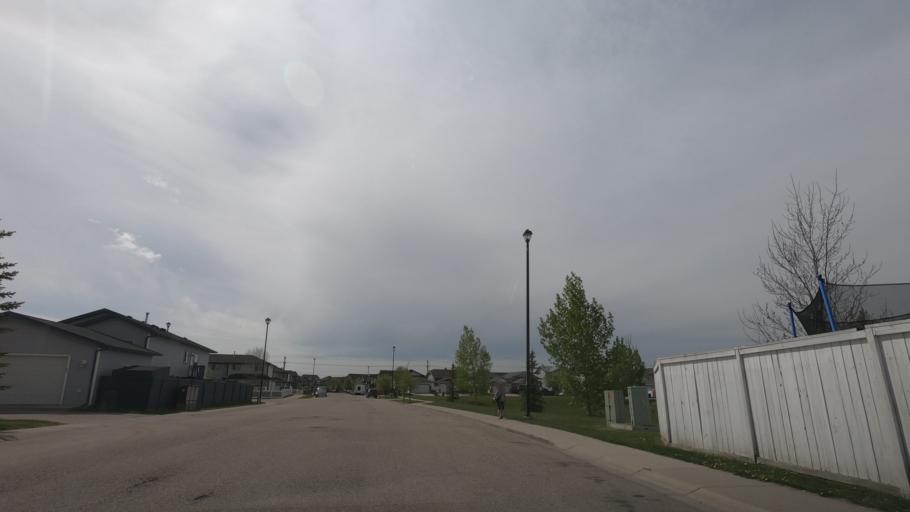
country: CA
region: Alberta
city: Airdrie
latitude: 51.3044
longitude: -114.0228
